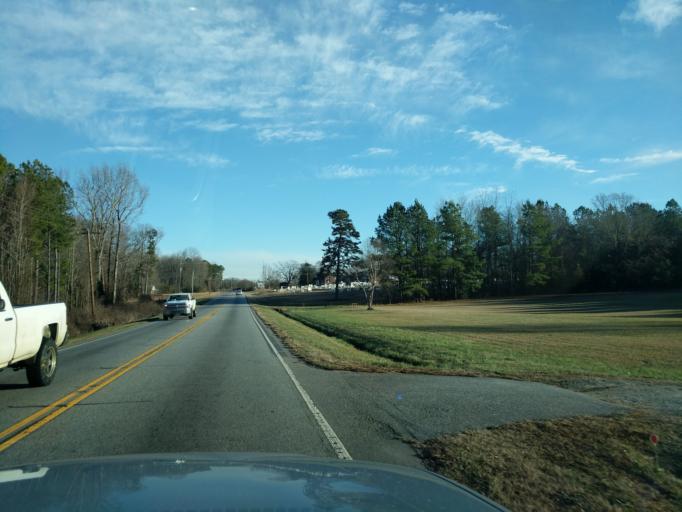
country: US
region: South Carolina
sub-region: Anderson County
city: Piedmont
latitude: 34.6722
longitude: -82.5300
